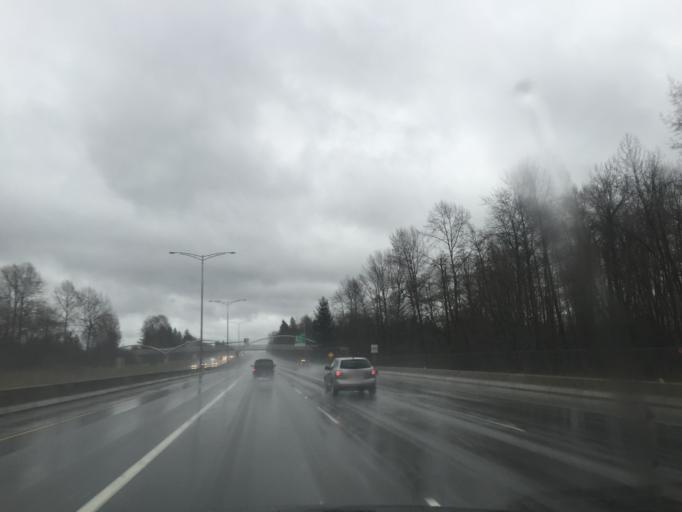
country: CA
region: British Columbia
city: Pitt Meadows
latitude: 49.1880
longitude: -122.7620
